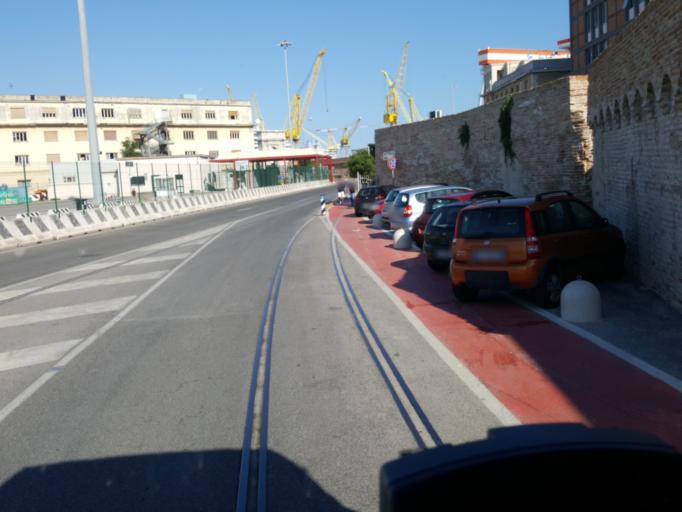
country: IT
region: The Marches
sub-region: Provincia di Ancona
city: Le Grazie di Ancona
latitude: 43.6238
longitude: 13.5090
